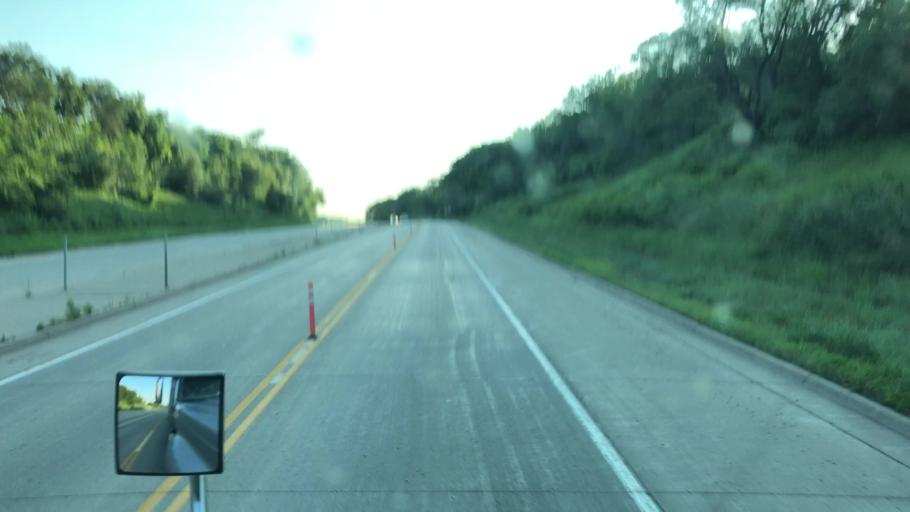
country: US
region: Minnesota
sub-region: Scott County
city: Belle Plaine
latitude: 44.6000
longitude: -93.8007
